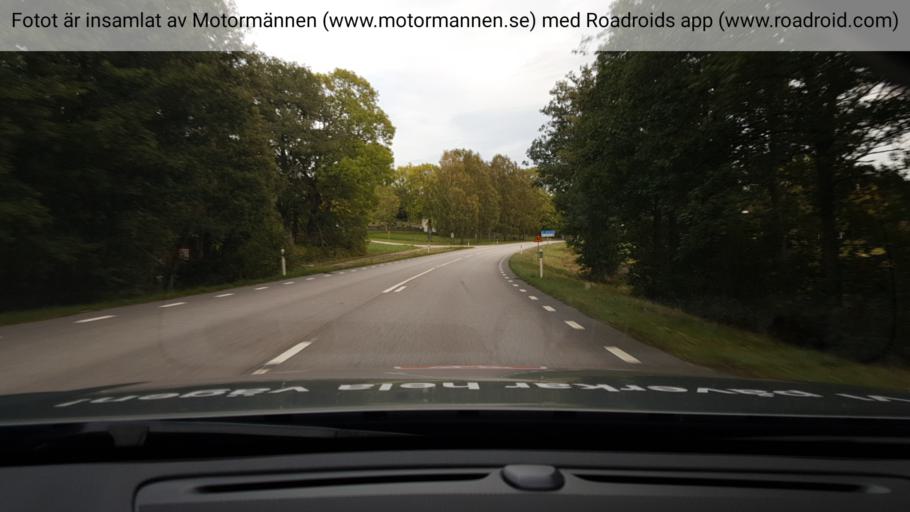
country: SE
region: Vaestra Goetaland
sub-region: Bengtsfors Kommun
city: Dals Langed
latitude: 59.0578
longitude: 12.4596
